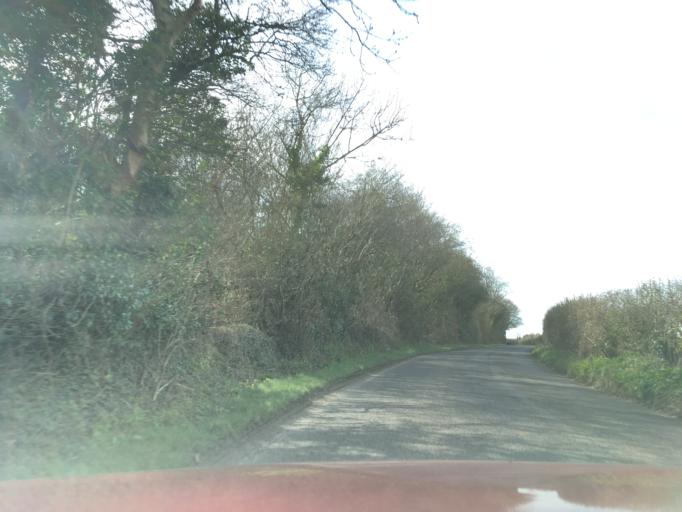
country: GB
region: England
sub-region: Wiltshire
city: Norton
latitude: 51.5204
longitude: -2.1480
